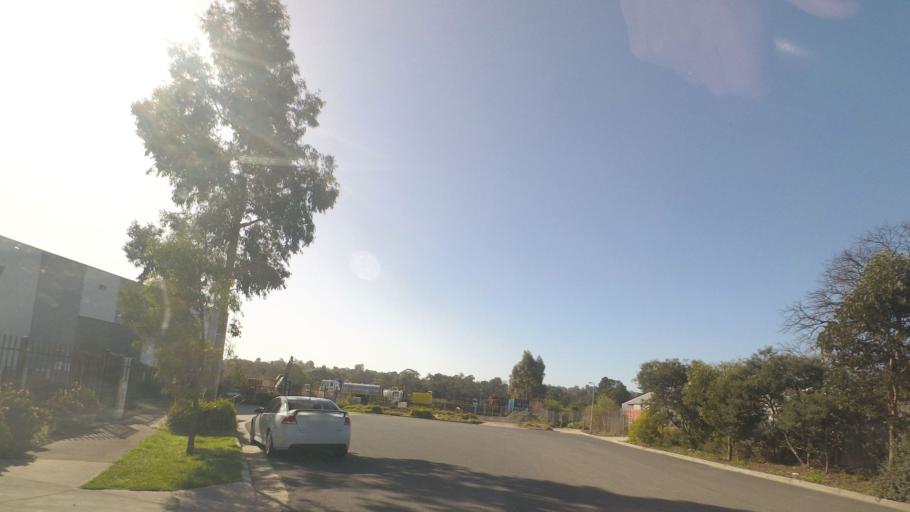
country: AU
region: Victoria
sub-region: Maroondah
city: Heathmont
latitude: -37.8412
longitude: 145.2476
